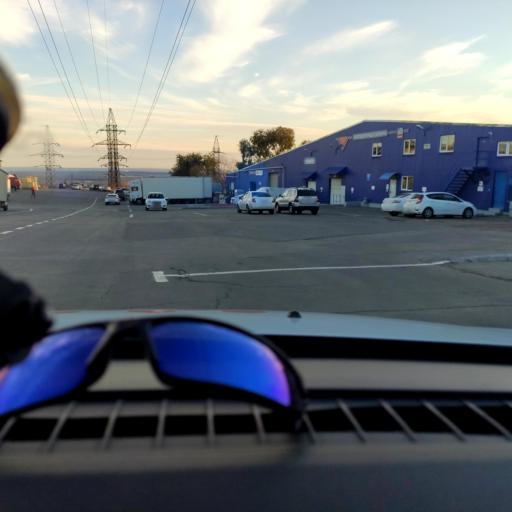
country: RU
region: Samara
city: Samara
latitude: 53.1822
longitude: 50.1744
